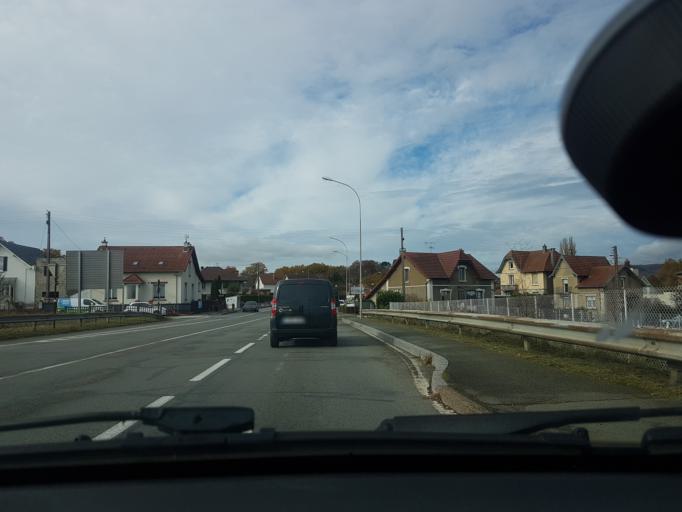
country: FR
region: Franche-Comte
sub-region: Territoire de Belfort
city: Danjoutin
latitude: 47.6188
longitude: 6.8513
